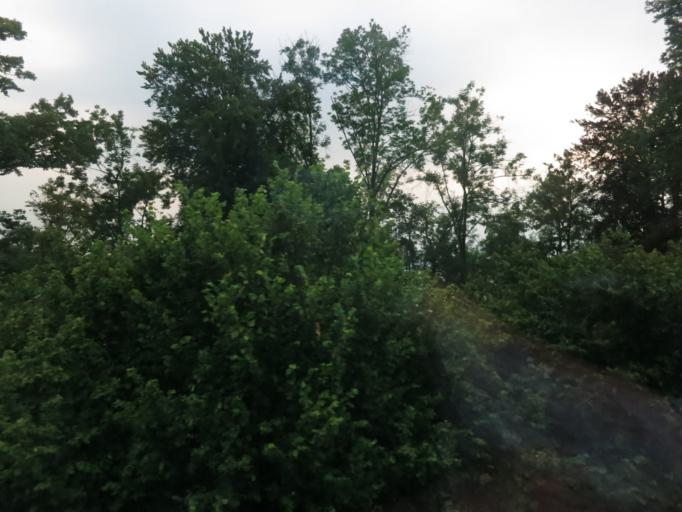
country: CH
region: Schwyz
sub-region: Bezirk March
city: Altendorf
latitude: 47.2011
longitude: 8.8083
